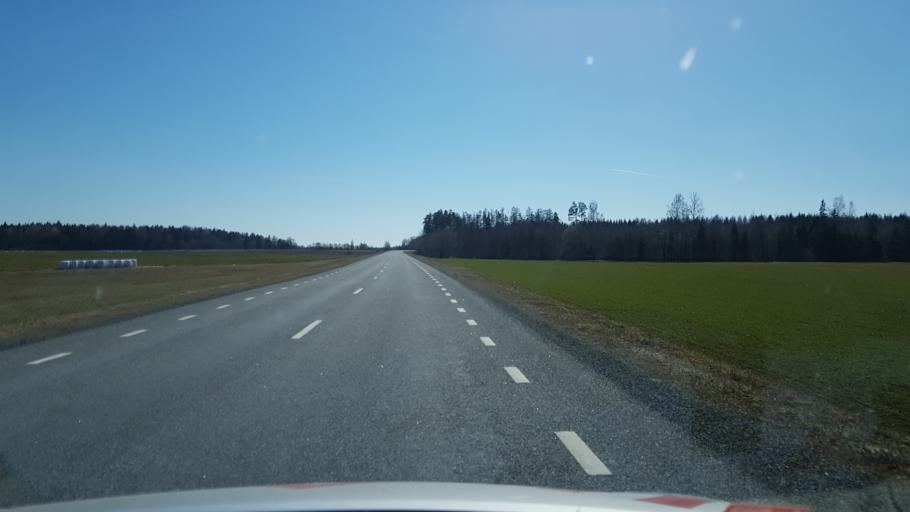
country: EE
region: Jaervamaa
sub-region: Jaerva-Jaani vald
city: Jarva-Jaani
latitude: 59.0940
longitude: 25.9792
